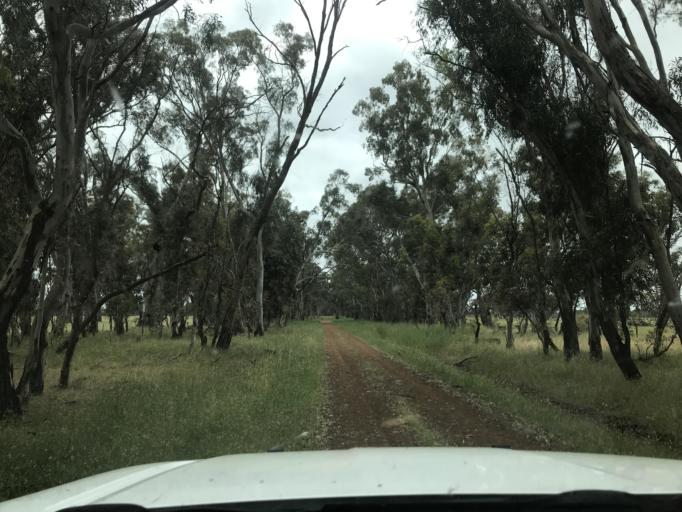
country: AU
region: South Australia
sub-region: Wattle Range
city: Penola
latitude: -37.2439
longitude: 141.1222
